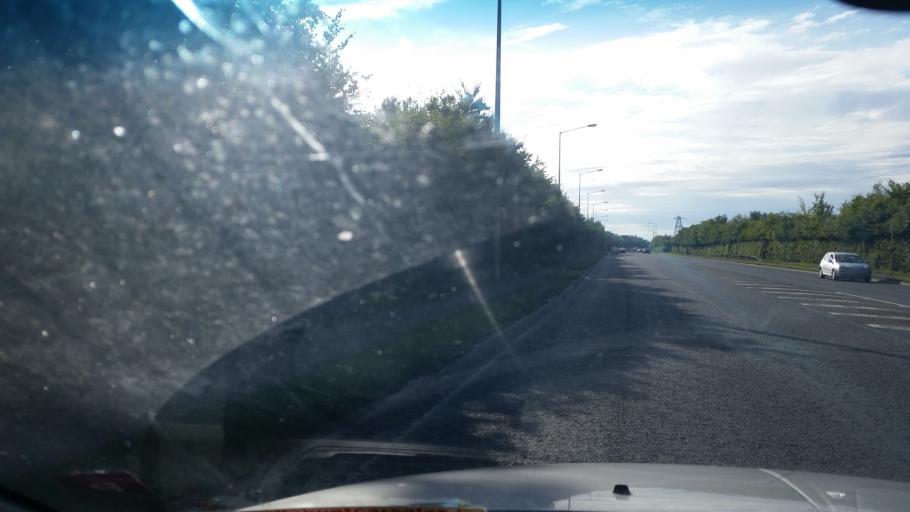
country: IE
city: Darndale
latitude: 53.4041
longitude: -6.1842
